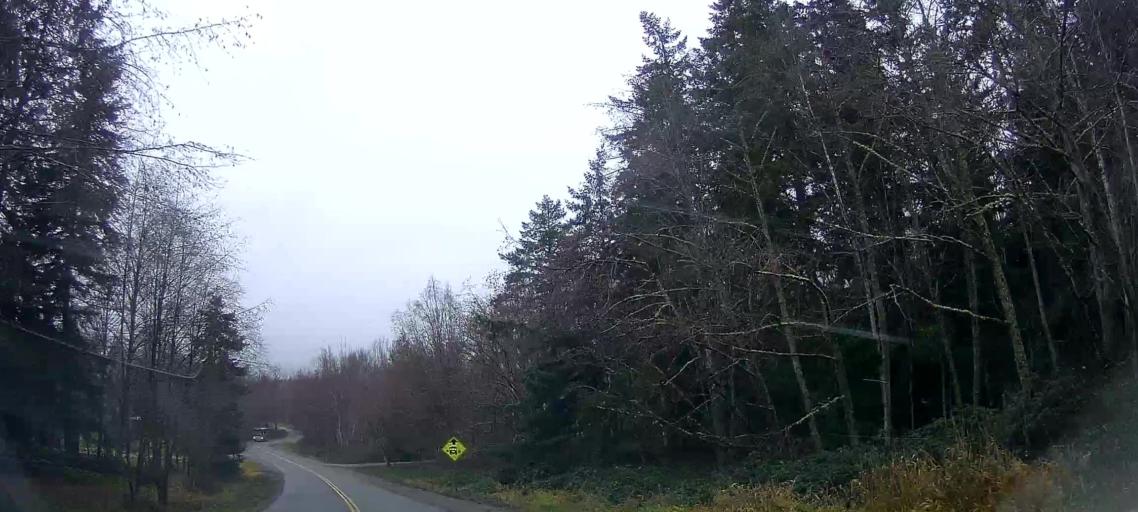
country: US
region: Washington
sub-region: Skagit County
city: Mount Vernon
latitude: 48.3807
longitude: -122.3019
